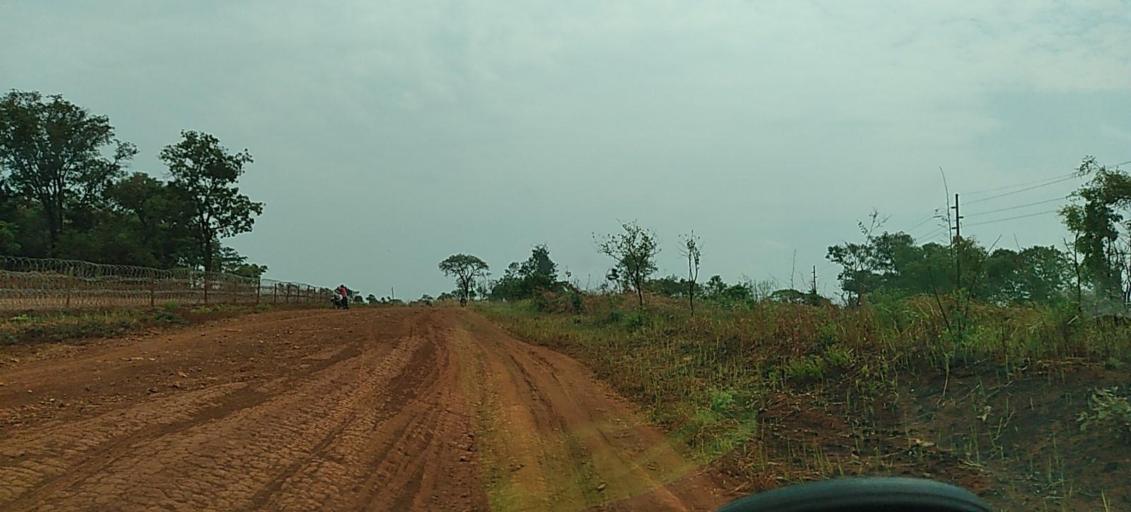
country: ZM
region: North-Western
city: Kansanshi
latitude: -12.0959
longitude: 26.4927
